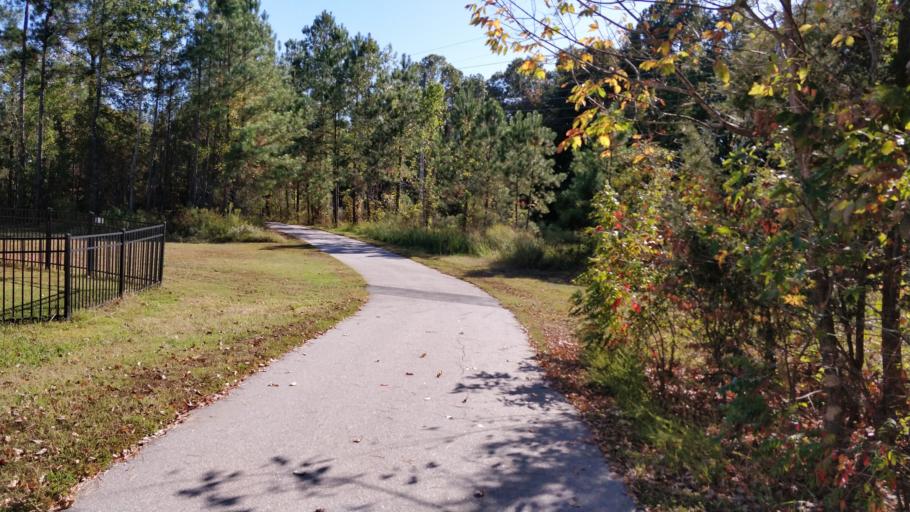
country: US
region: North Carolina
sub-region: Wake County
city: Morrisville
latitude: 35.8310
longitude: -78.8417
